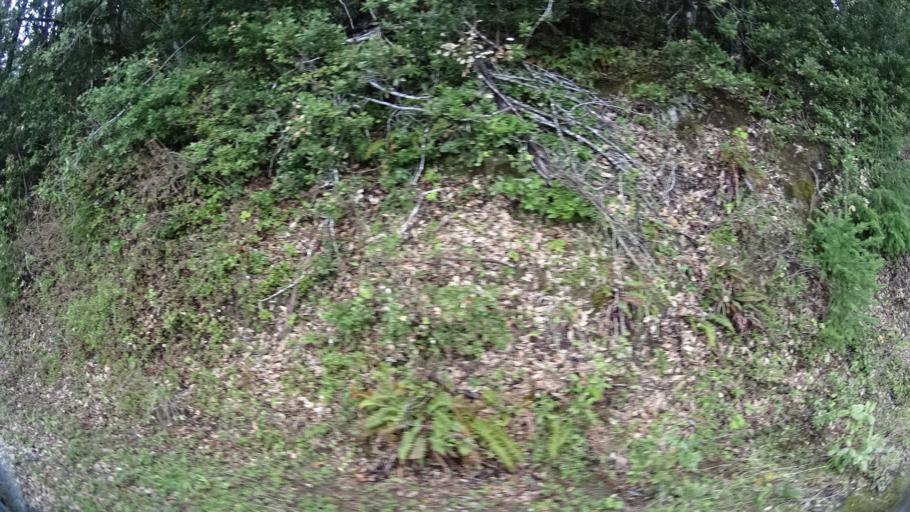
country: US
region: California
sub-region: Humboldt County
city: Blue Lake
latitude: 40.8720
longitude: -123.8937
